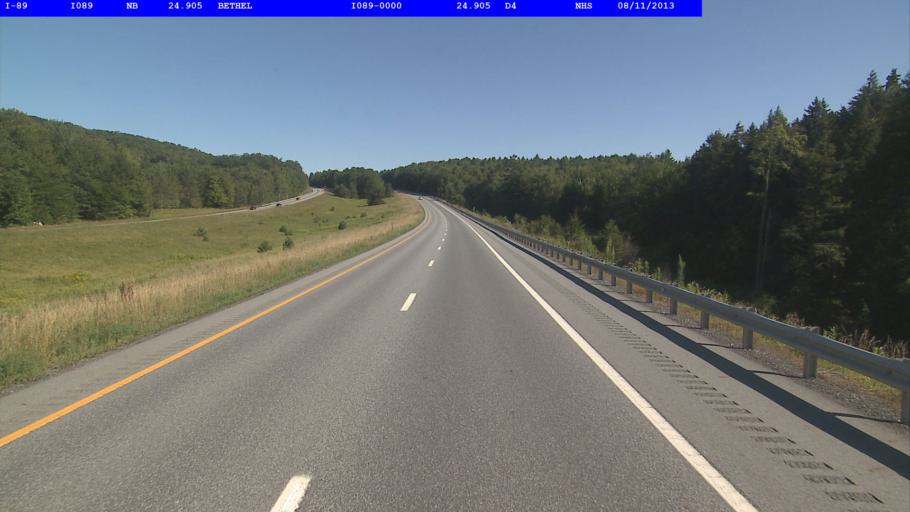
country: US
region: Vermont
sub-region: Orange County
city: Randolph
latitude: 43.8600
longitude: -72.6069
